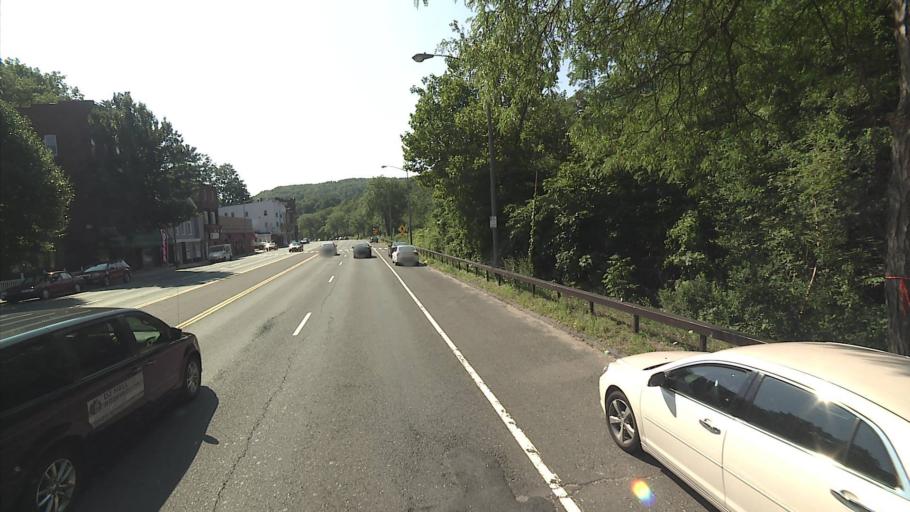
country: US
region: Connecticut
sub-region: Litchfield County
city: Winsted
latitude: 41.9225
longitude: -73.0754
